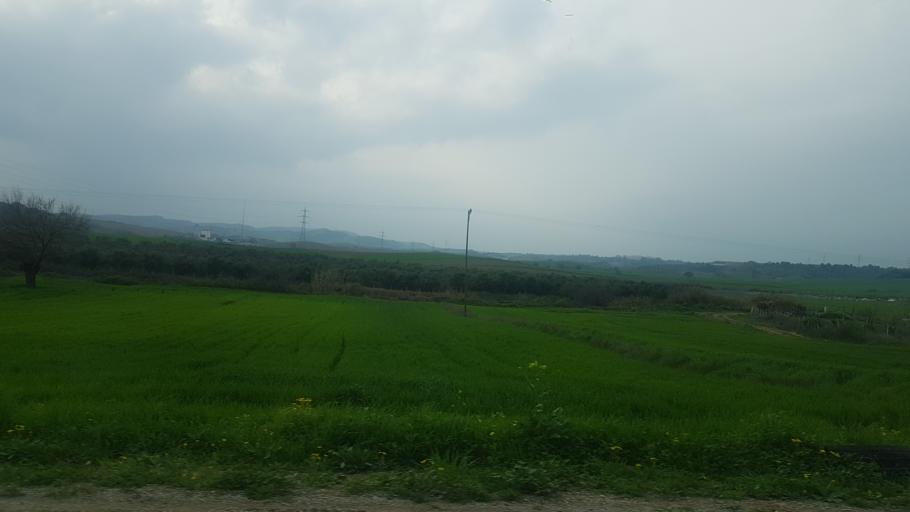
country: TR
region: Mersin
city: Yenice
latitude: 37.0624
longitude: 35.1701
